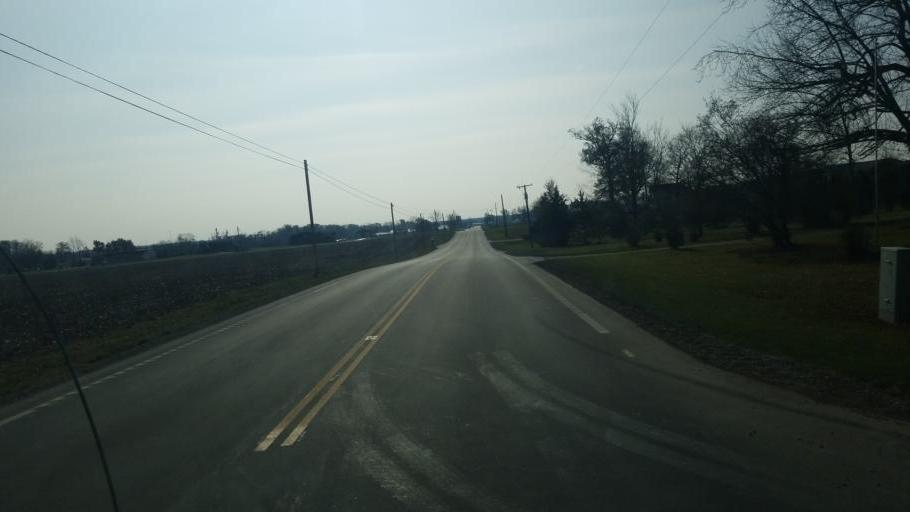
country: US
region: Ohio
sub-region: Mercer County
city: Fort Recovery
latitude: 40.4321
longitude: -84.7846
